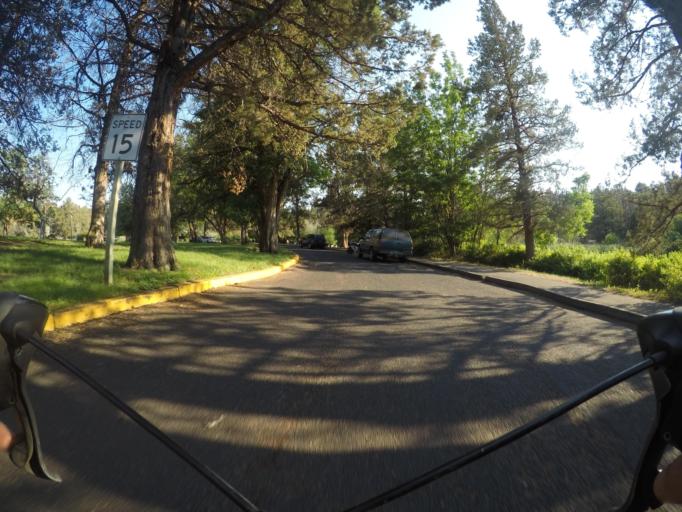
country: US
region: Oregon
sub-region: Deschutes County
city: Redmond
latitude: 44.2691
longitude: -121.2568
